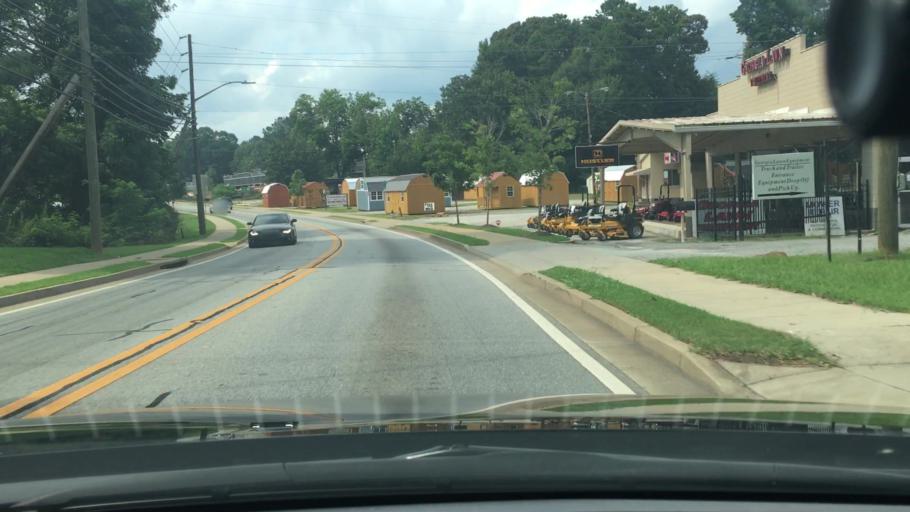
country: US
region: Georgia
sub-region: Coweta County
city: East Newnan
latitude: 33.3586
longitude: -84.7910
